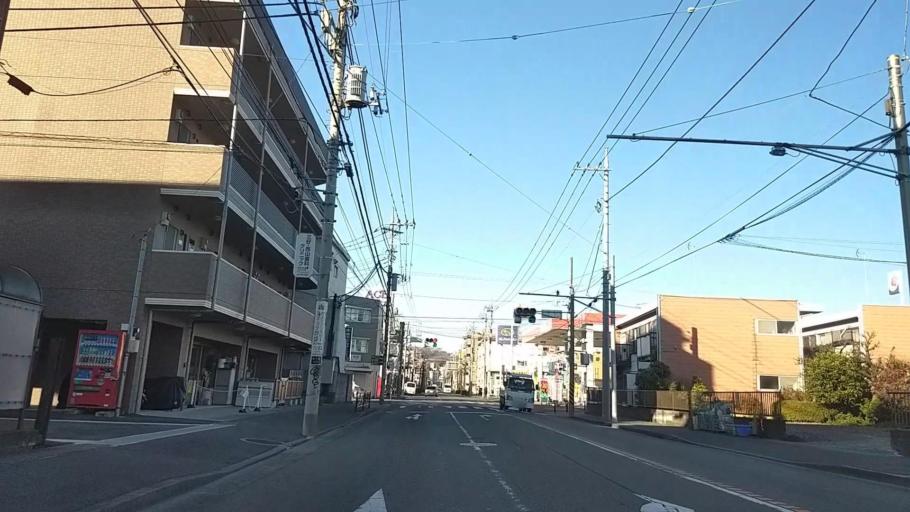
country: JP
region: Tokyo
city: Chofugaoka
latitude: 35.6120
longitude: 139.5768
